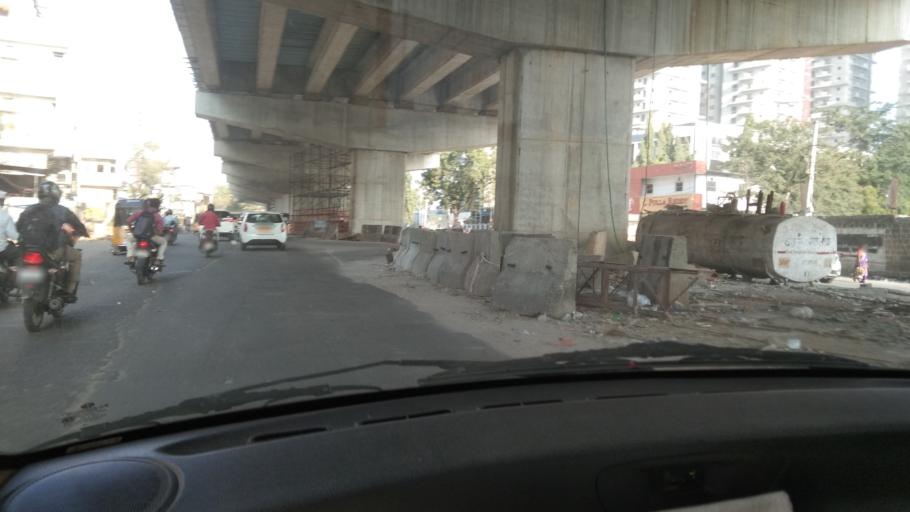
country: IN
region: Telangana
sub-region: Hyderabad
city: Hyderabad
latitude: 17.4104
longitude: 78.3977
